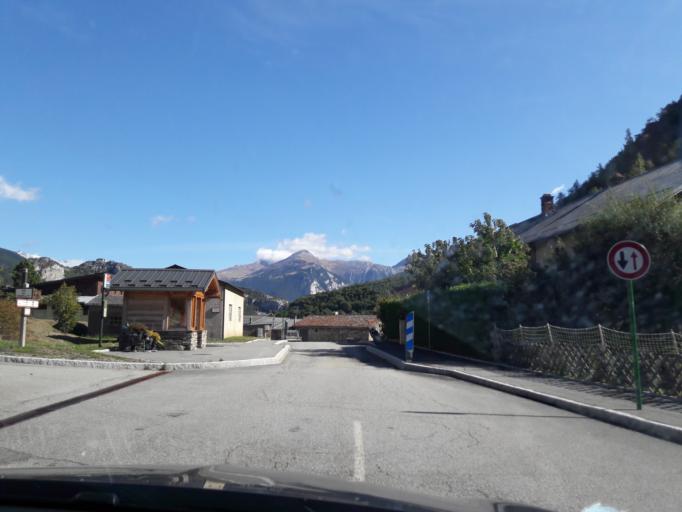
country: FR
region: Rhone-Alpes
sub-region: Departement de la Savoie
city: Modane
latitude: 45.2071
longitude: 6.7076
